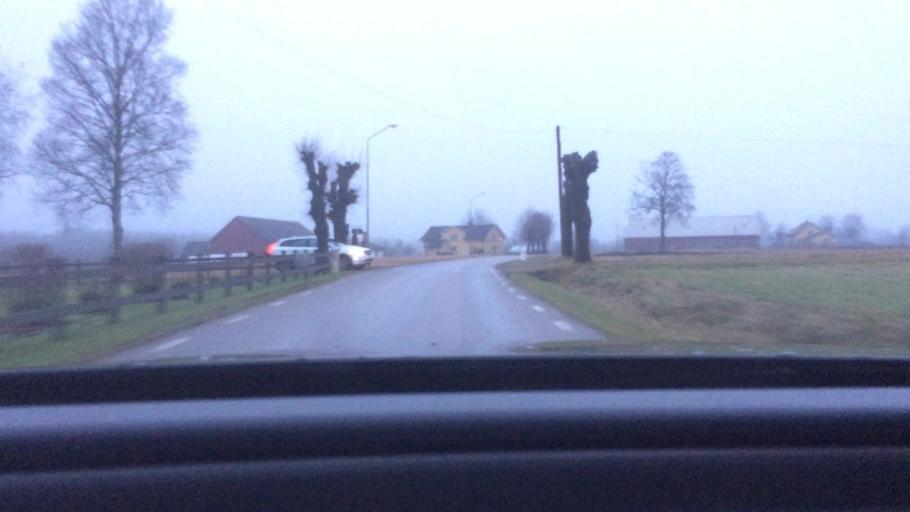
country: SE
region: Vaestra Goetaland
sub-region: Ulricehamns Kommun
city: Ulricehamn
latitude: 57.9500
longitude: 13.3861
